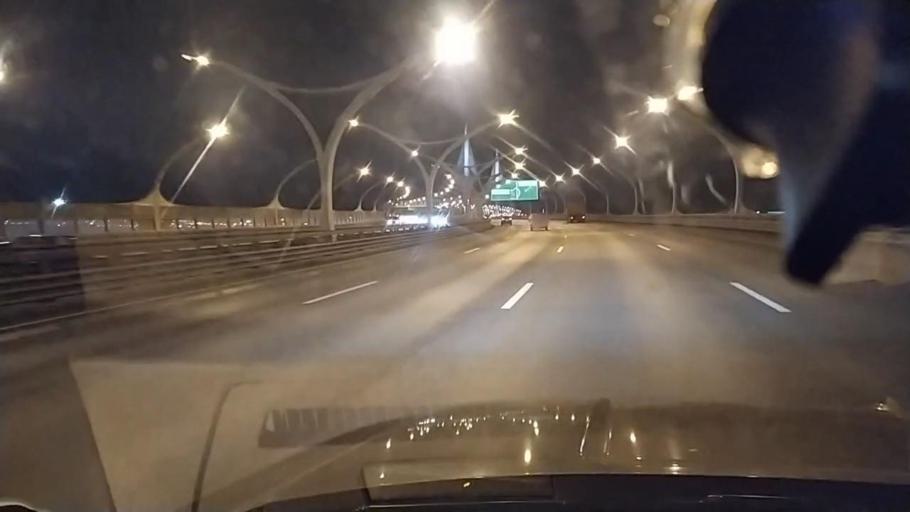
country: RU
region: St.-Petersburg
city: Staraya Derevnya
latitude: 59.9740
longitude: 30.2130
